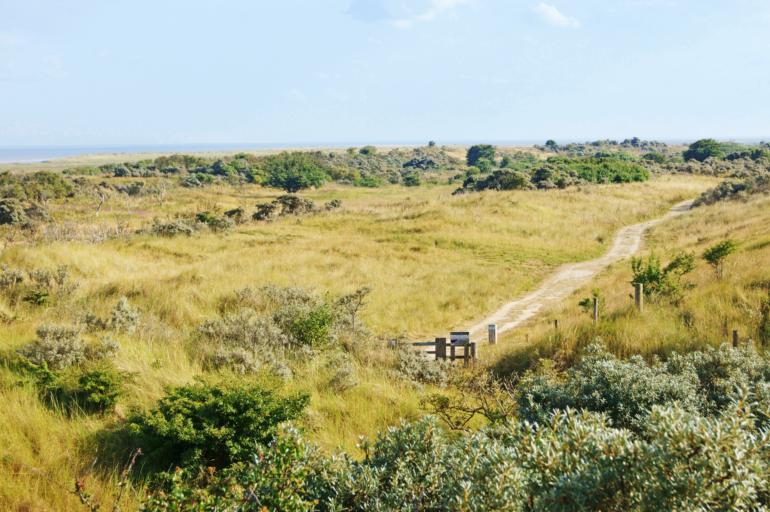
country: GB
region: England
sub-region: Lincolnshire
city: Skegness
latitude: 53.1008
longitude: 0.3344
